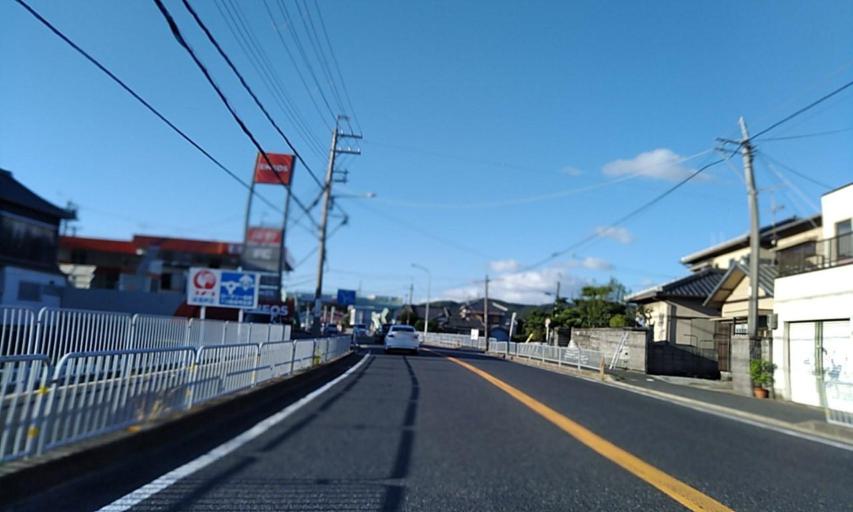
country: JP
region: Wakayama
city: Wakayama-shi
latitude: 34.3211
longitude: 135.1506
